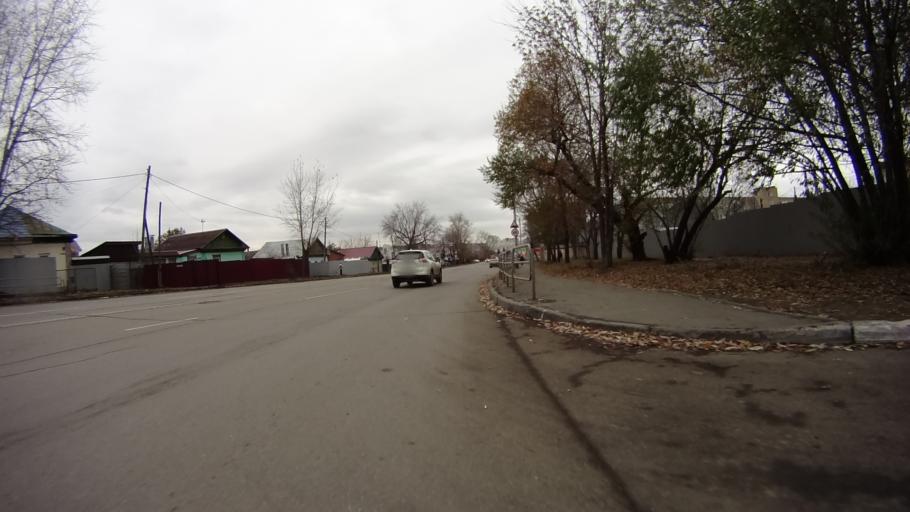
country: RU
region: Chelyabinsk
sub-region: Gorod Chelyabinsk
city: Chelyabinsk
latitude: 55.1900
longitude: 61.3626
